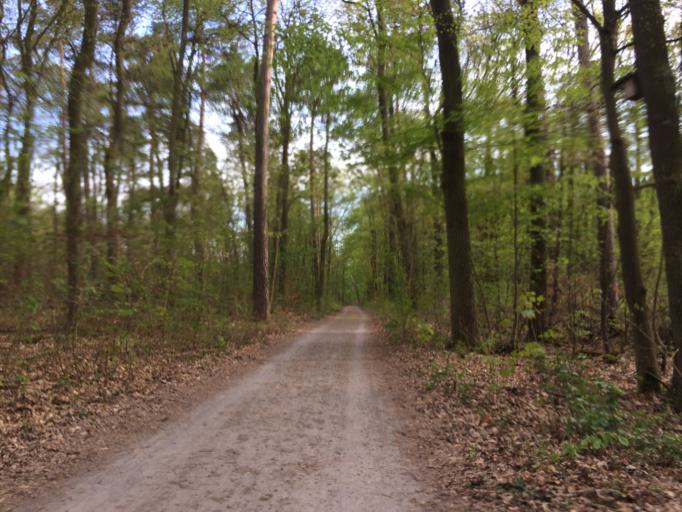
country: DE
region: Berlin
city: Buch
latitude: 52.6449
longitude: 13.4840
